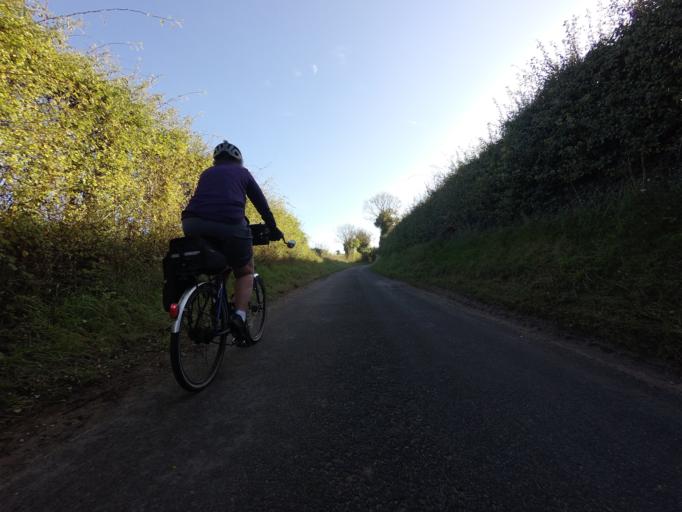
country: GB
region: England
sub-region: Norfolk
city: Dersingham
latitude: 52.8209
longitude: 0.5249
